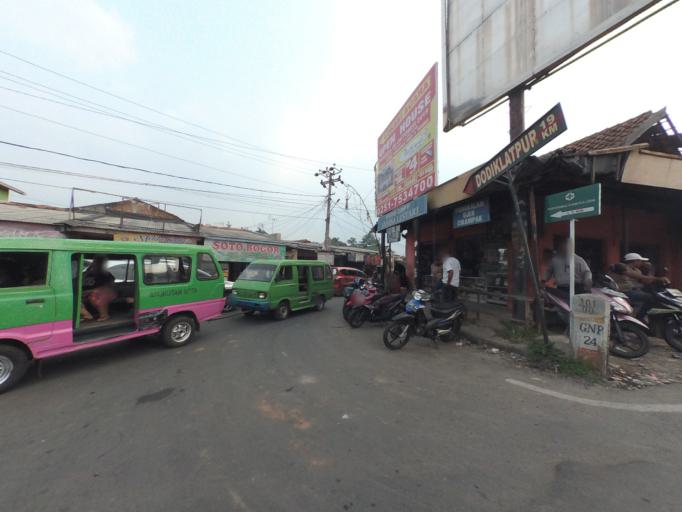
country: ID
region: West Java
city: Ciampea
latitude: -6.5569
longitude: 106.6940
